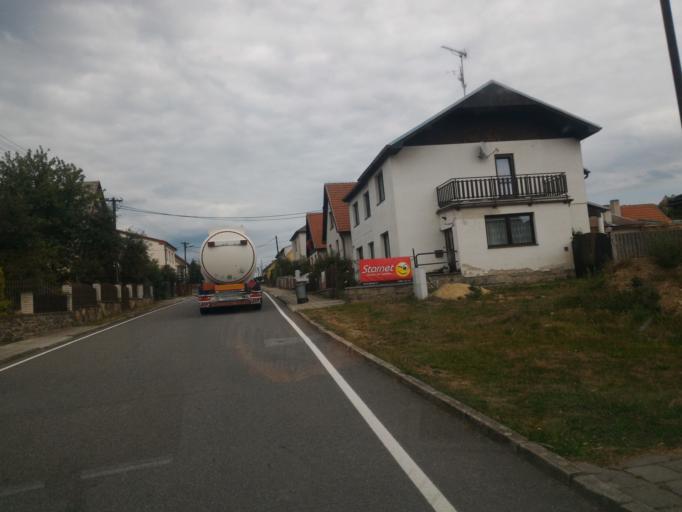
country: CZ
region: Vysocina
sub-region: Okres Jihlava
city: Telc
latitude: 49.1362
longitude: 15.5569
